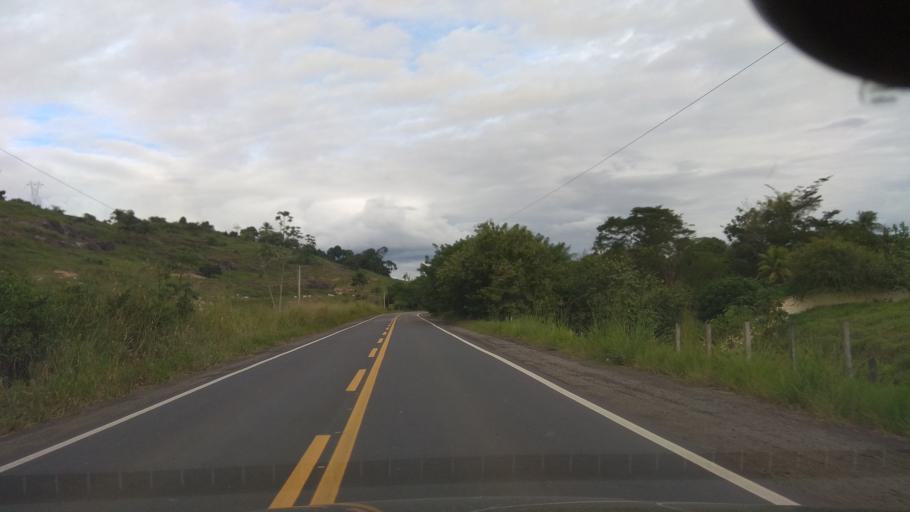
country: BR
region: Bahia
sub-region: Ipiau
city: Ipiau
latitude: -14.1820
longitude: -39.6631
